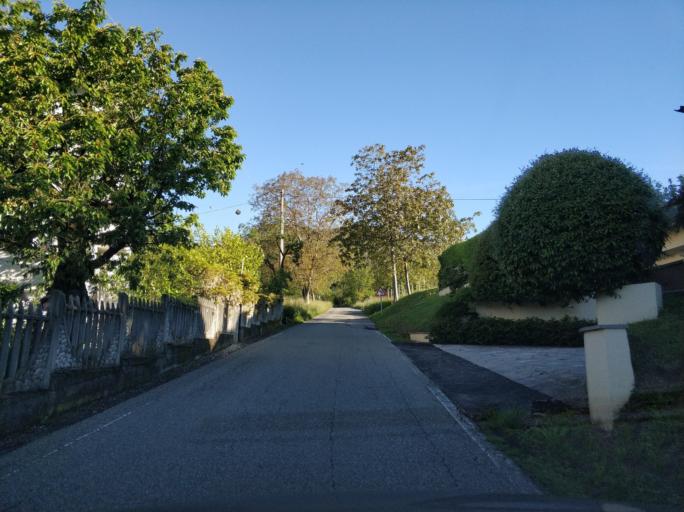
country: IT
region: Piedmont
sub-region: Provincia di Torino
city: Coassolo
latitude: 45.2968
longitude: 7.4691
